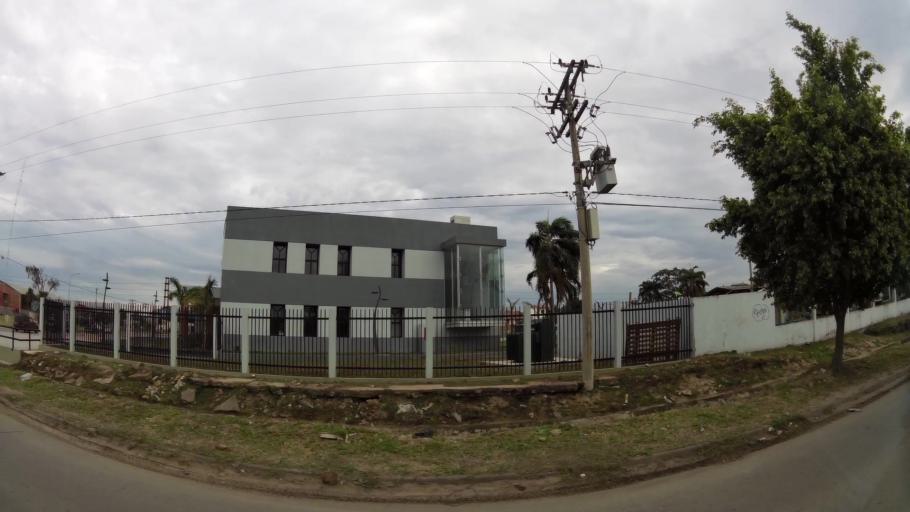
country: BO
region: Santa Cruz
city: Santa Cruz de la Sierra
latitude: -17.7422
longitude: -63.1650
